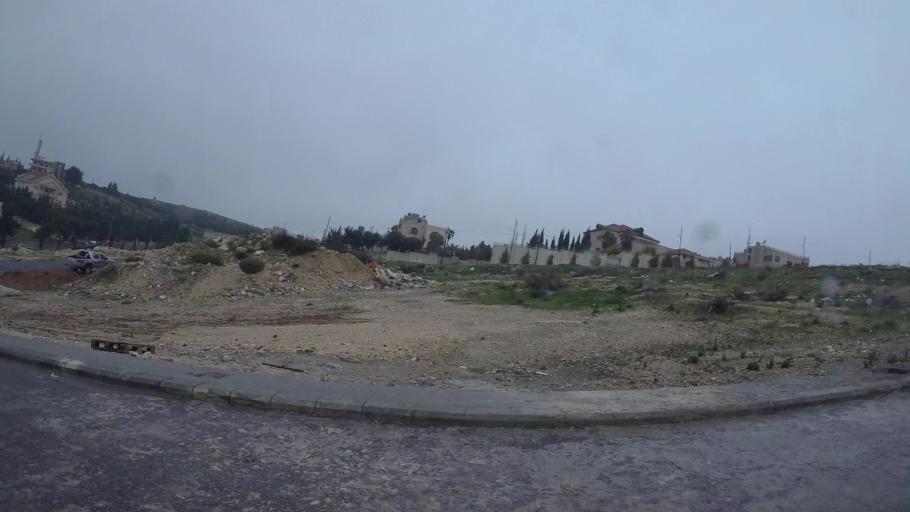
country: JO
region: Amman
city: Wadi as Sir
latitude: 31.9982
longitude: 35.8122
